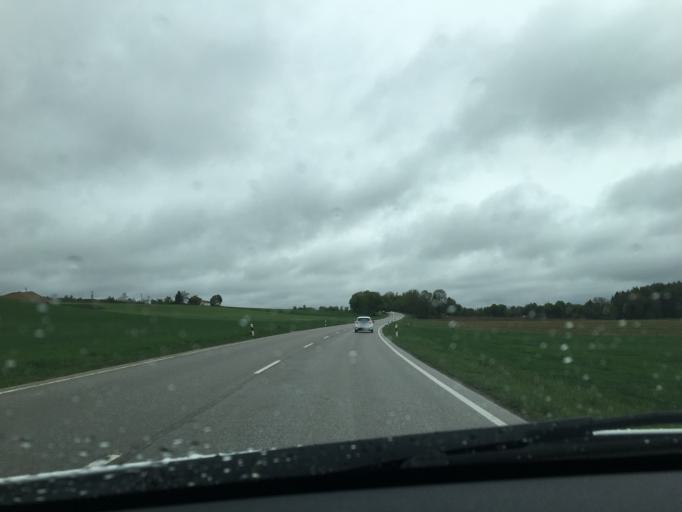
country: DE
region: Bavaria
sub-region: Upper Bavaria
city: Icking
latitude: 47.9642
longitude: 11.4452
